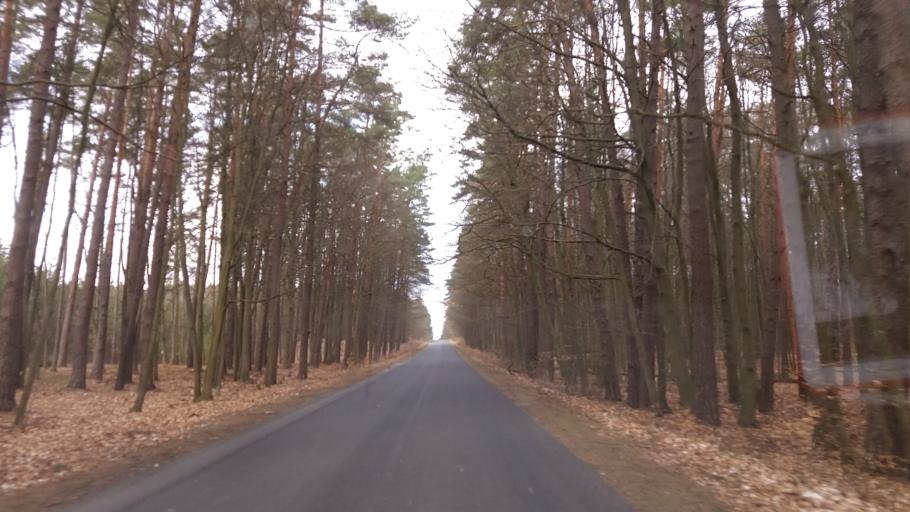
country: PL
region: West Pomeranian Voivodeship
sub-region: Powiat choszczenski
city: Recz
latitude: 53.2035
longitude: 15.6297
